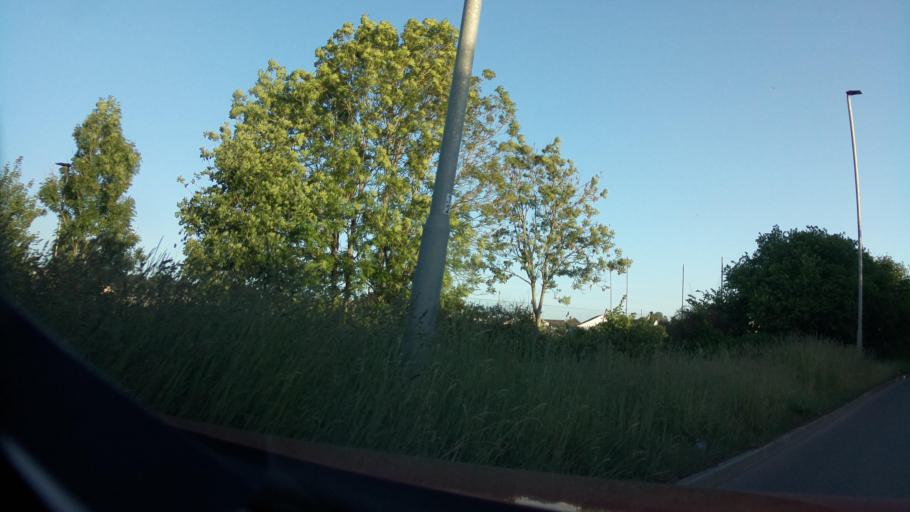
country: GB
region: England
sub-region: Devon
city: Kingsteignton
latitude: 50.5592
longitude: -3.6016
